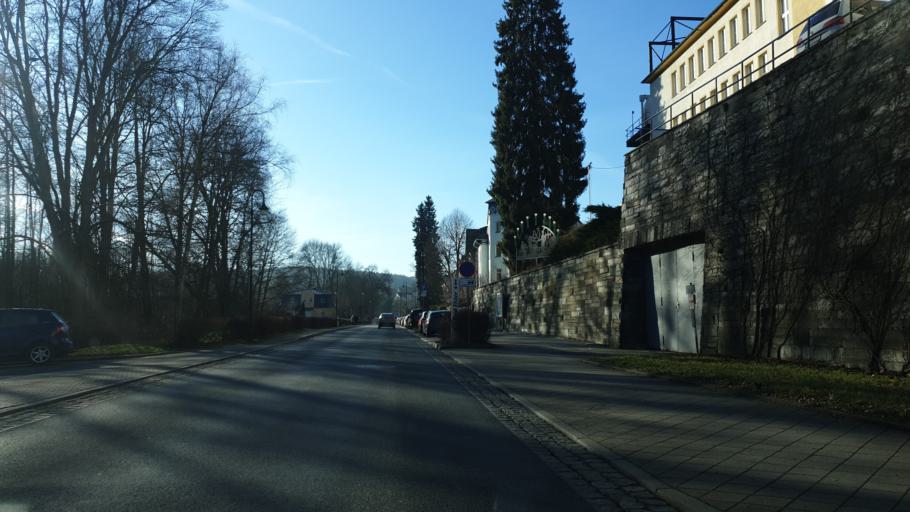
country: DE
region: Saxony
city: Bad Elster
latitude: 50.2883
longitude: 12.2404
